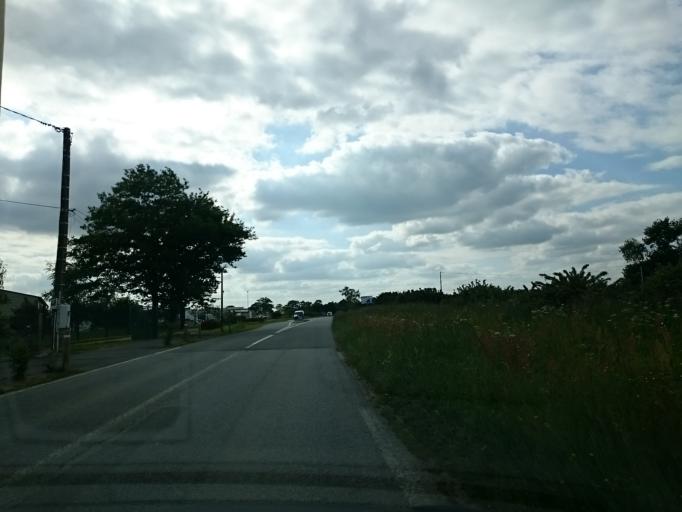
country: FR
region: Brittany
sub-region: Departement d'Ille-et-Vilaine
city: Laille
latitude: 47.9746
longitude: -1.6983
